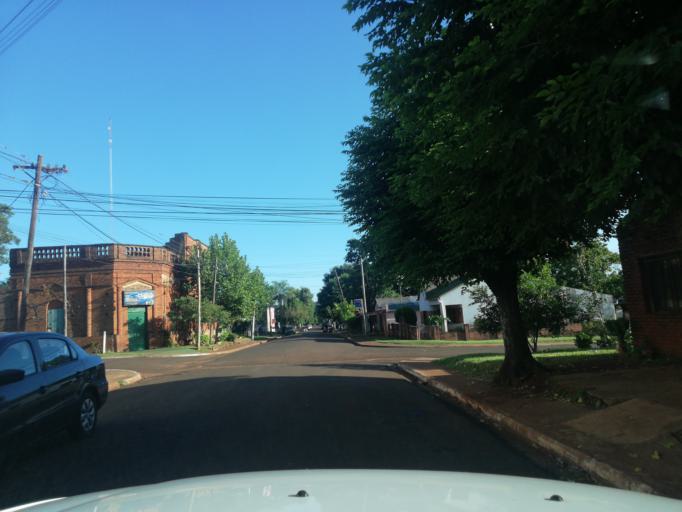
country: AR
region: Misiones
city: Garupa
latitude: -27.4822
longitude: -55.8281
